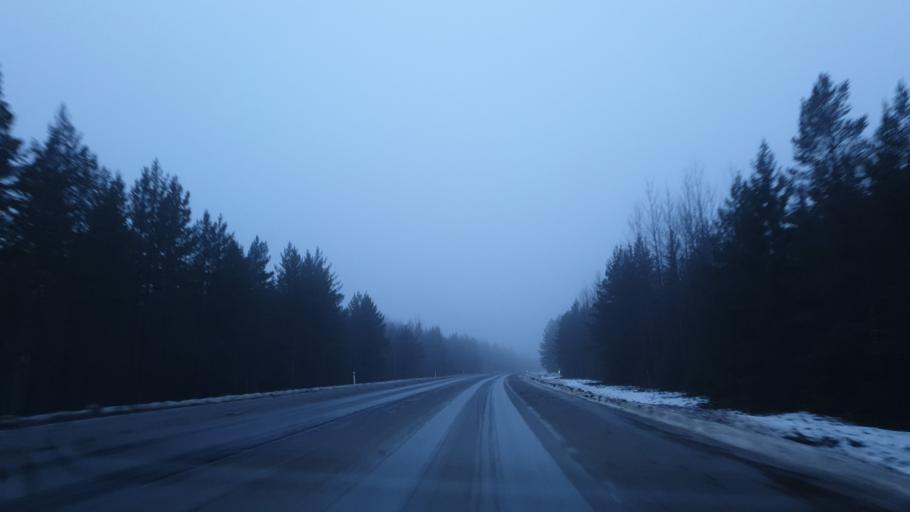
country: SE
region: Vaesterbotten
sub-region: Umea Kommun
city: Holmsund
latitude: 63.7592
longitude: 20.3479
